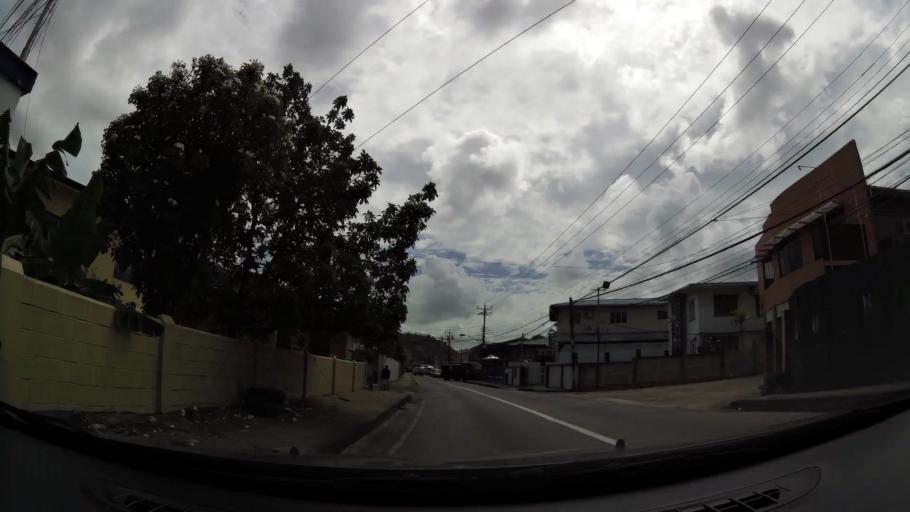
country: TT
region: Diego Martin
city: Petit Valley
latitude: 10.6948
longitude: -61.5563
